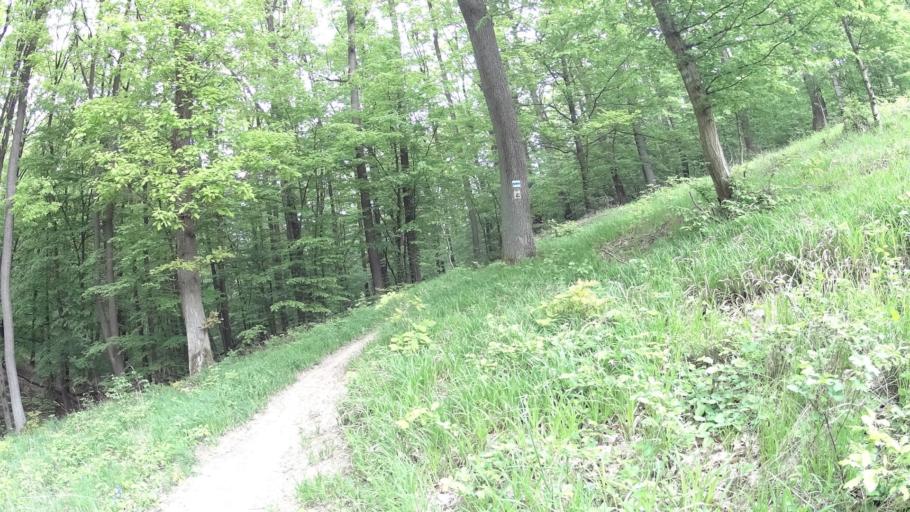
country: HU
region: Nograd
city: Romhany
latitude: 47.9010
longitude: 19.2417
